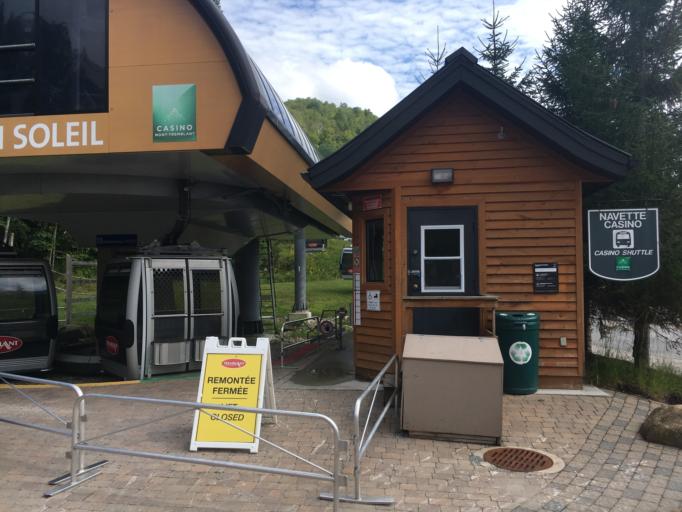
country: CA
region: Quebec
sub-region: Laurentides
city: Mont-Tremblant
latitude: 46.2123
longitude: -74.5829
